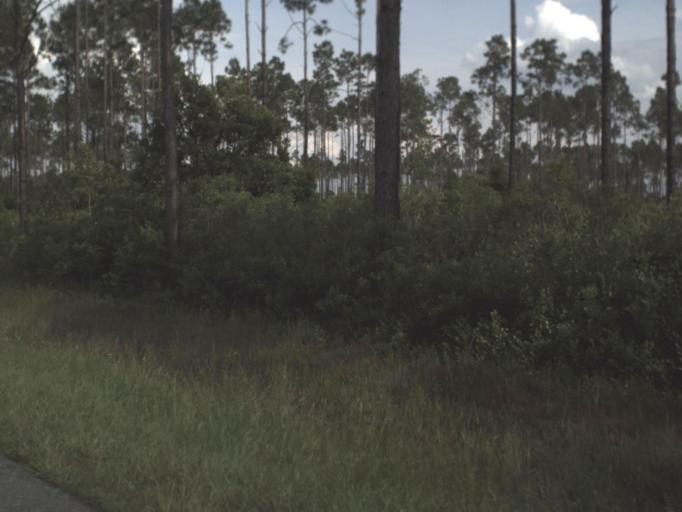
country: US
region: Florida
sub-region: Baker County
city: Macclenny
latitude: 30.5674
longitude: -82.4205
